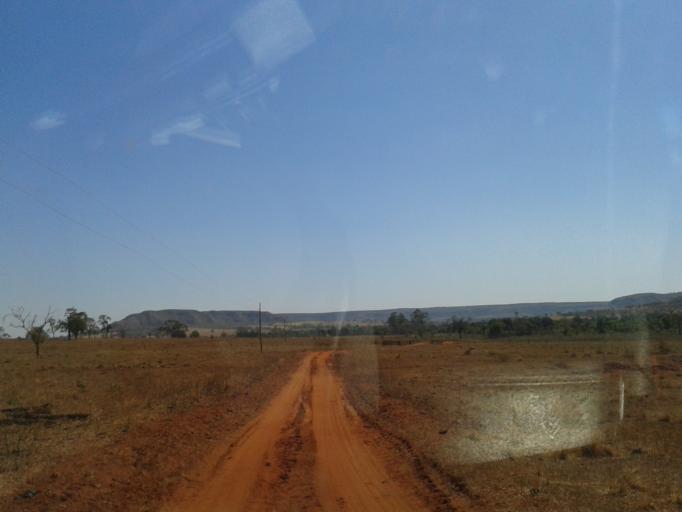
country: BR
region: Minas Gerais
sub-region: Santa Vitoria
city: Santa Vitoria
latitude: -19.0716
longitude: -50.0419
